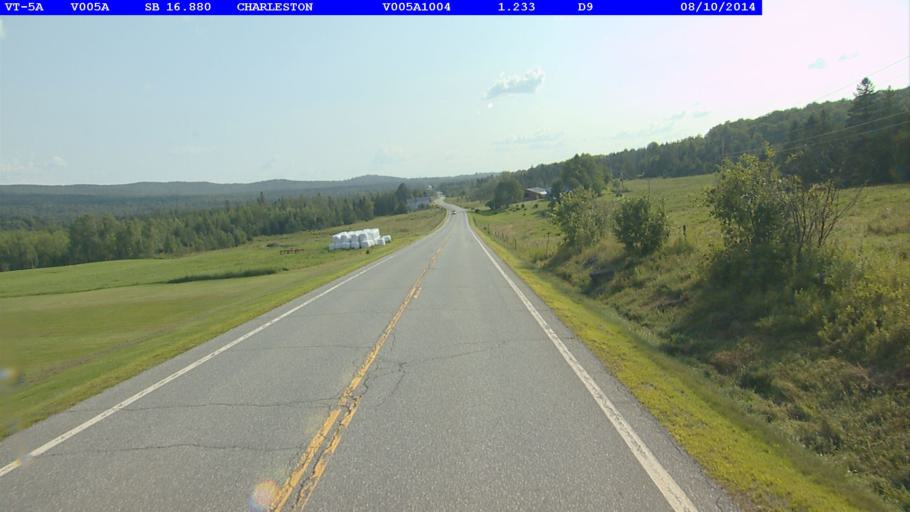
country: US
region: Vermont
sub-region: Orleans County
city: Newport
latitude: 44.8509
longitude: -72.0549
